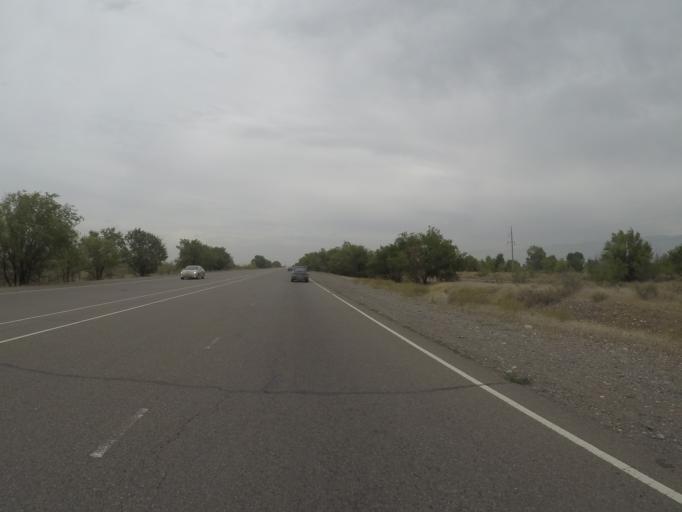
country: KG
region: Chuy
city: Tokmok
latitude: 42.8341
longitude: 75.4364
